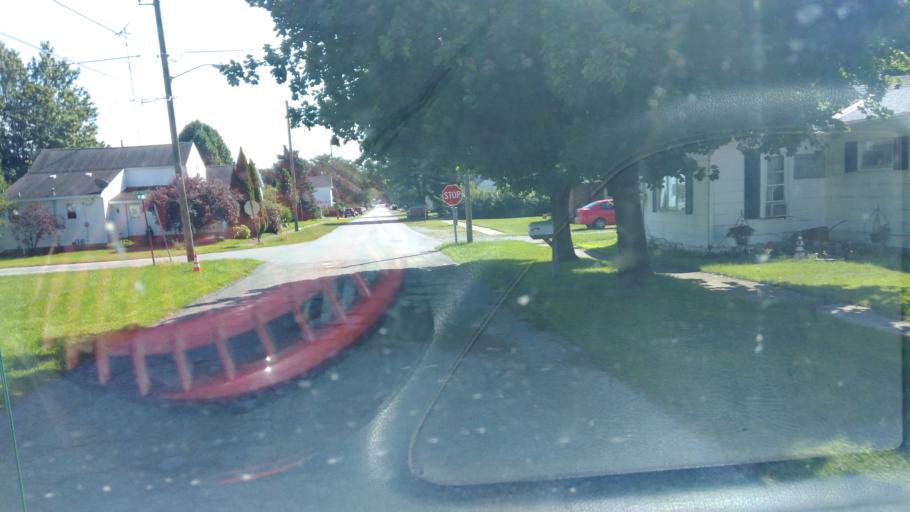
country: US
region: Ohio
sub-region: Hardin County
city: Ada
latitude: 40.7109
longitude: -83.8452
